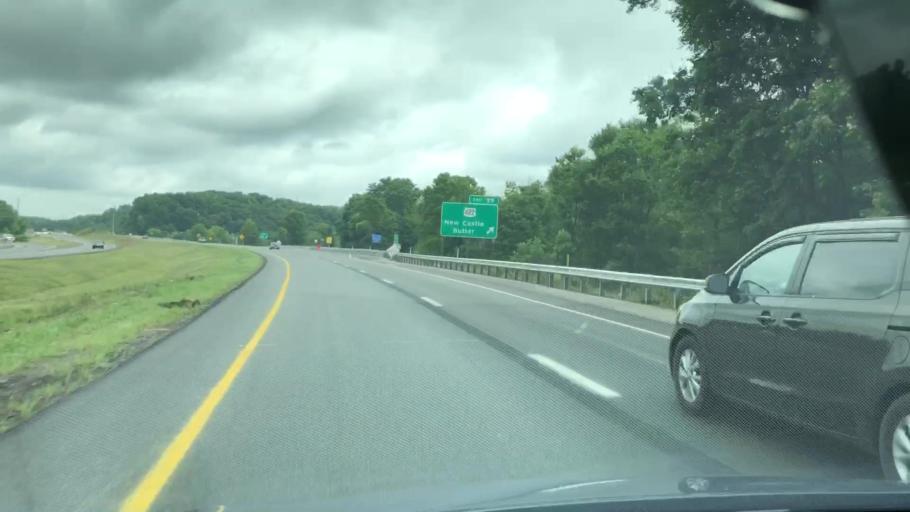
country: US
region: Pennsylvania
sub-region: Butler County
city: Prospect
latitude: 40.9583
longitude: -80.1366
